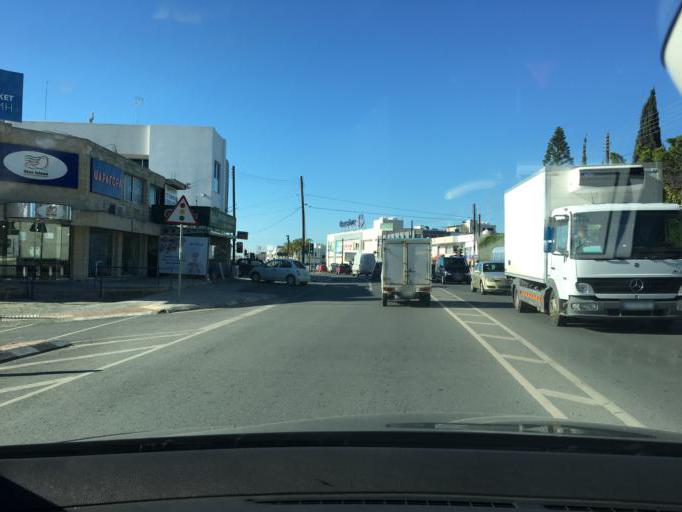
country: CY
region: Limassol
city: Mouttagiaka
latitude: 34.7022
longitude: 33.0784
